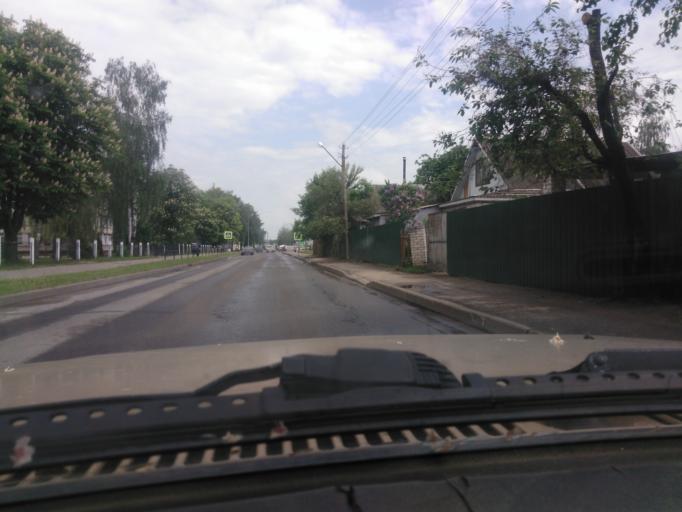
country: BY
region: Mogilev
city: Mahilyow
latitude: 53.9324
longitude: 30.3580
